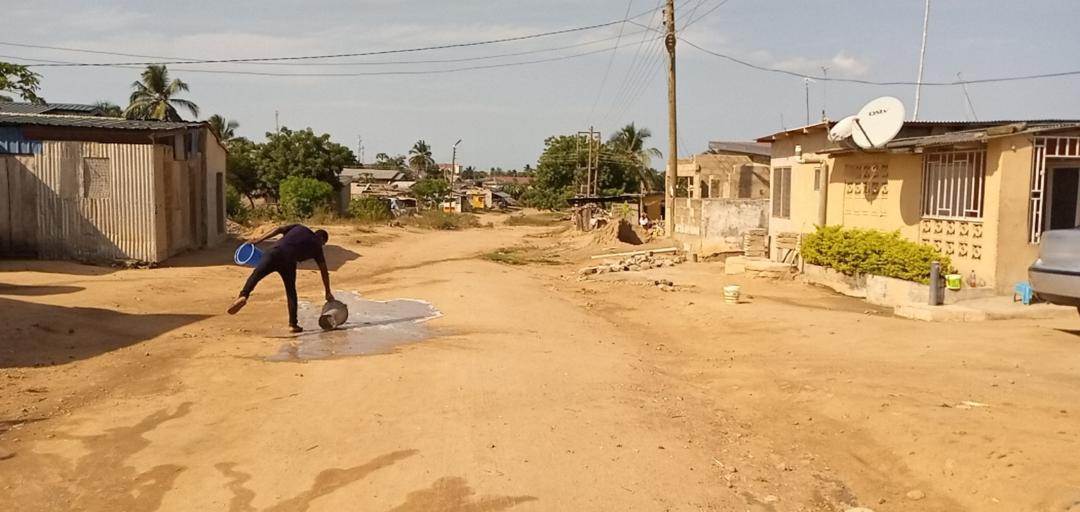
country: GH
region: Central
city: Winneba
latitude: 5.3549
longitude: -0.6200
